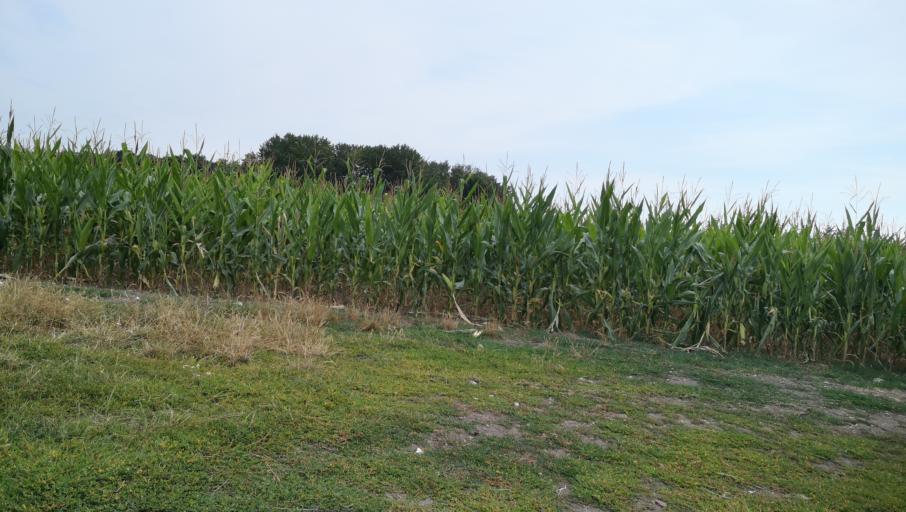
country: FR
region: Centre
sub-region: Departement du Loiret
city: Marigny-les-Usages
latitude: 47.9635
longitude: 2.0124
